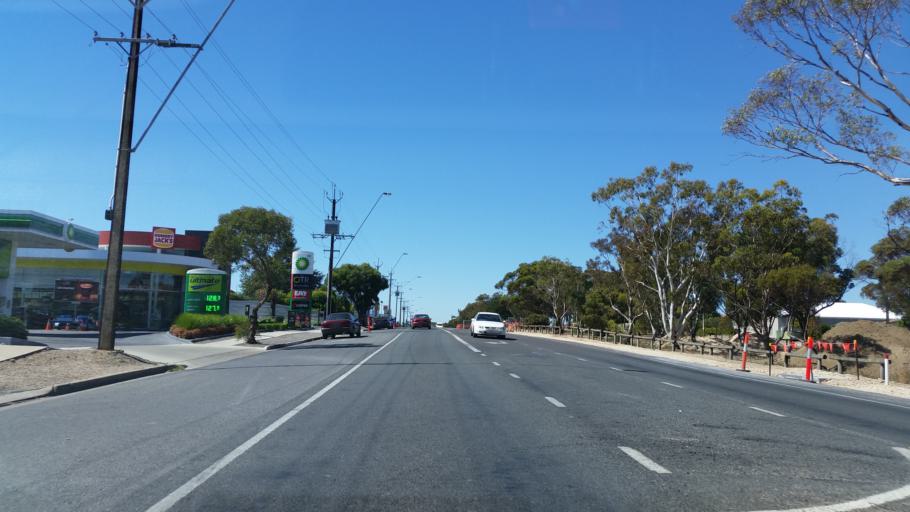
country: AU
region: South Australia
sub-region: Murray Bridge
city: Murray Bridge
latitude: -35.1294
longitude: 139.2504
